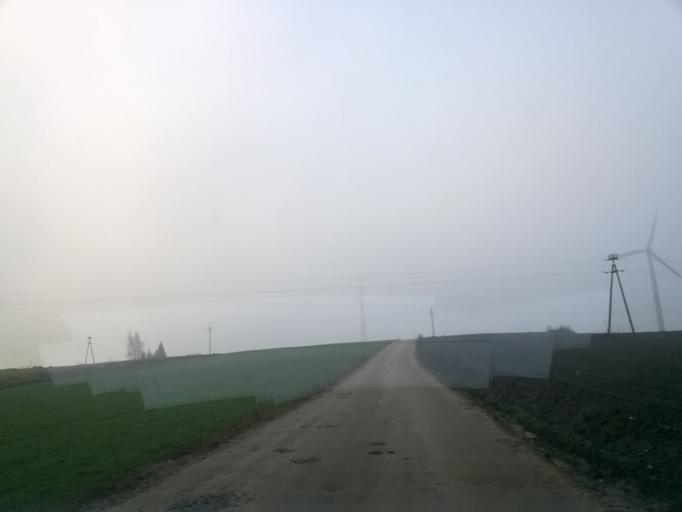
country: PL
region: Kujawsko-Pomorskie
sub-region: Powiat nakielski
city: Kcynia
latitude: 52.9877
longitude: 17.4828
